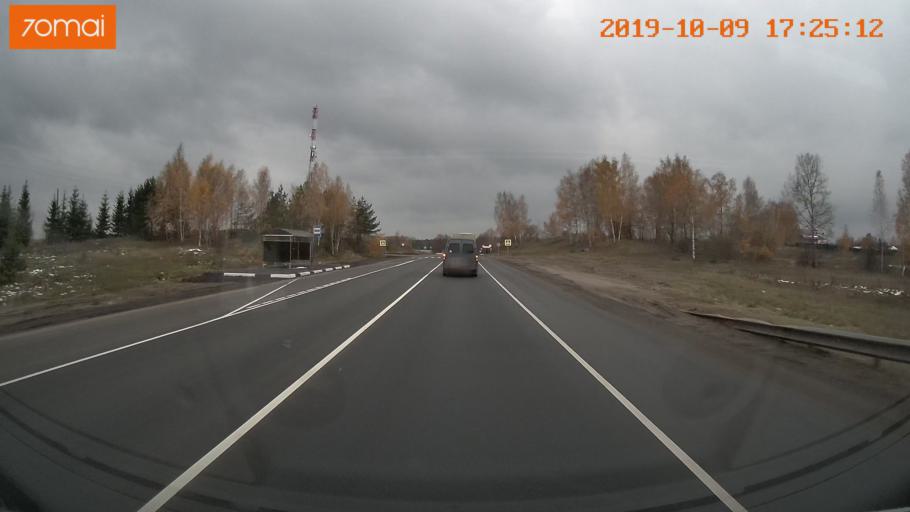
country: RU
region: Ivanovo
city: Furmanov
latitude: 57.1814
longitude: 41.0940
